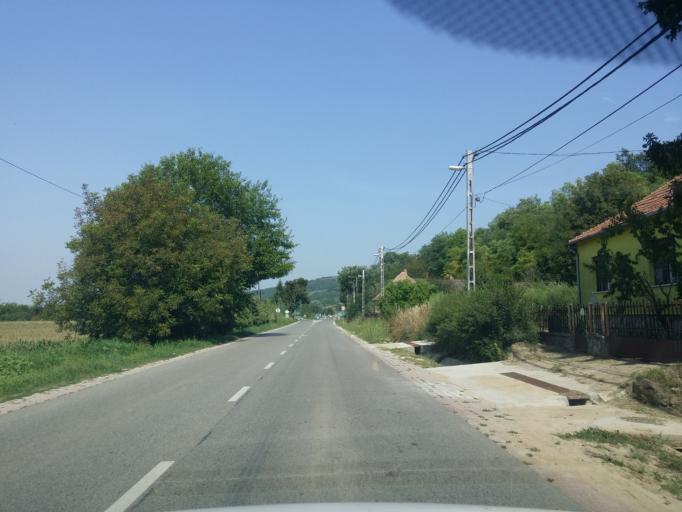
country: HU
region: Tolna
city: Pincehely
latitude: 46.6923
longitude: 18.4549
